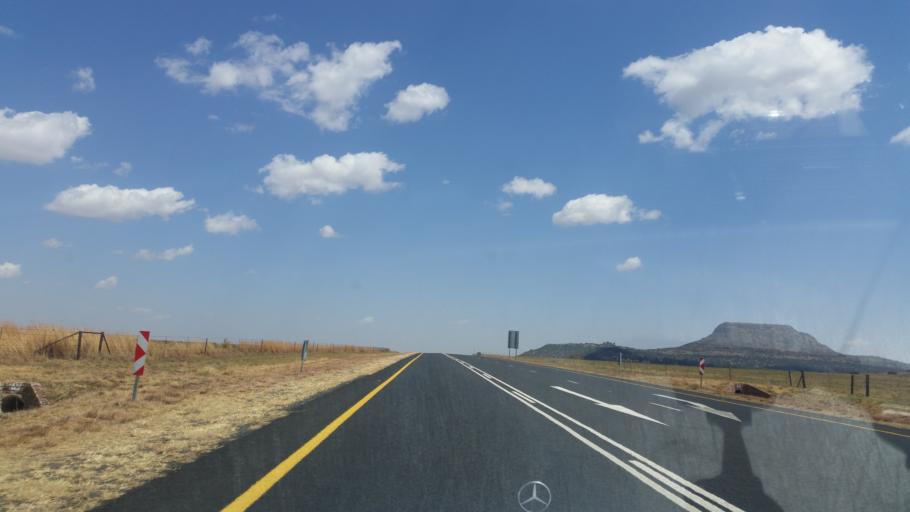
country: ZA
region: Orange Free State
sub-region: Thabo Mofutsanyana District Municipality
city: Senekal
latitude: -28.3037
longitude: 27.8028
